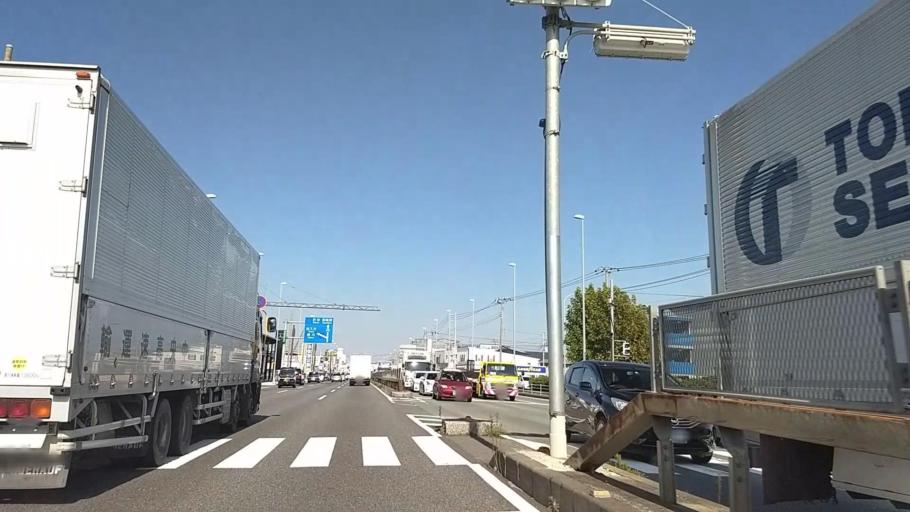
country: JP
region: Kanagawa
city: Atsugi
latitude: 35.4545
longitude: 139.3589
